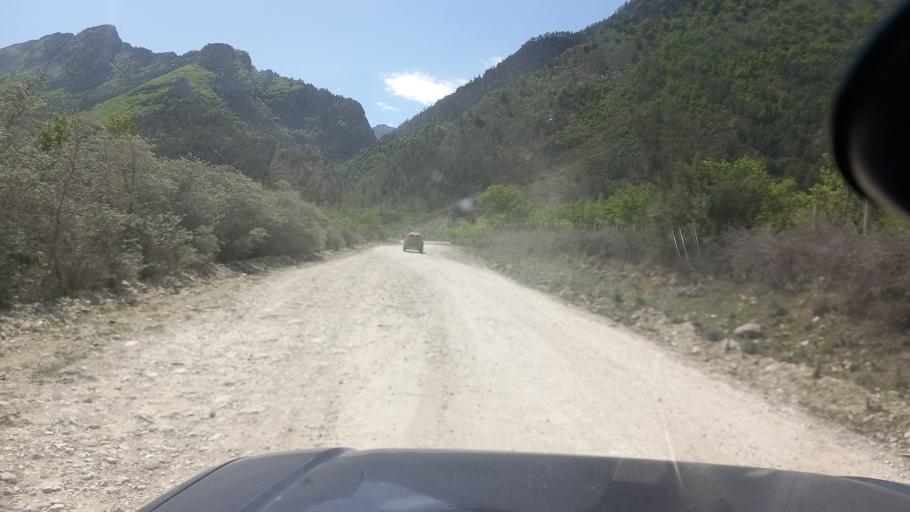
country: RU
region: Dagestan
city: Gunib
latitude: 42.4684
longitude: 46.8837
